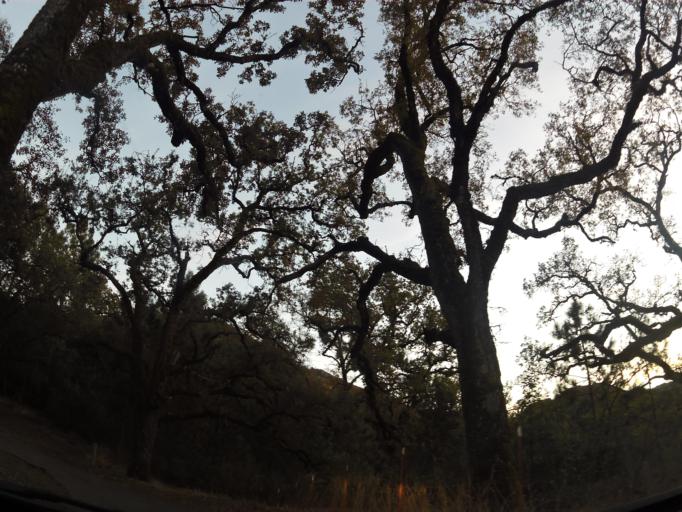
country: US
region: California
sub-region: San Benito County
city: San Juan Bautista
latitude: 36.7601
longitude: -121.5054
